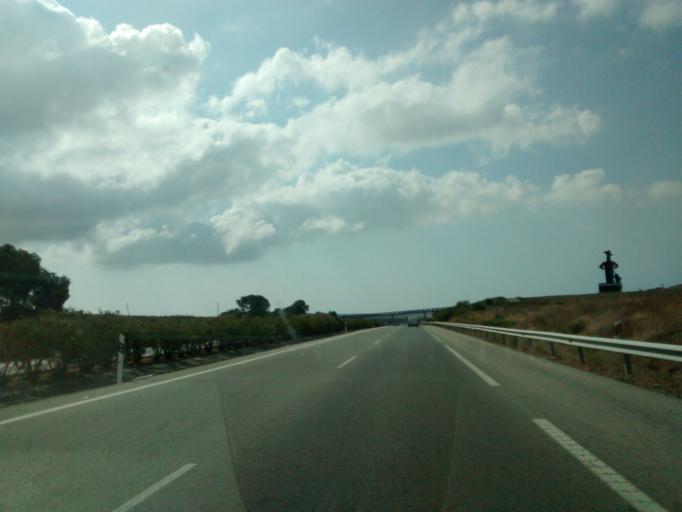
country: ES
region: Andalusia
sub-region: Provincia de Cadiz
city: Vejer de la Frontera
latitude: 36.2588
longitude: -6.0290
